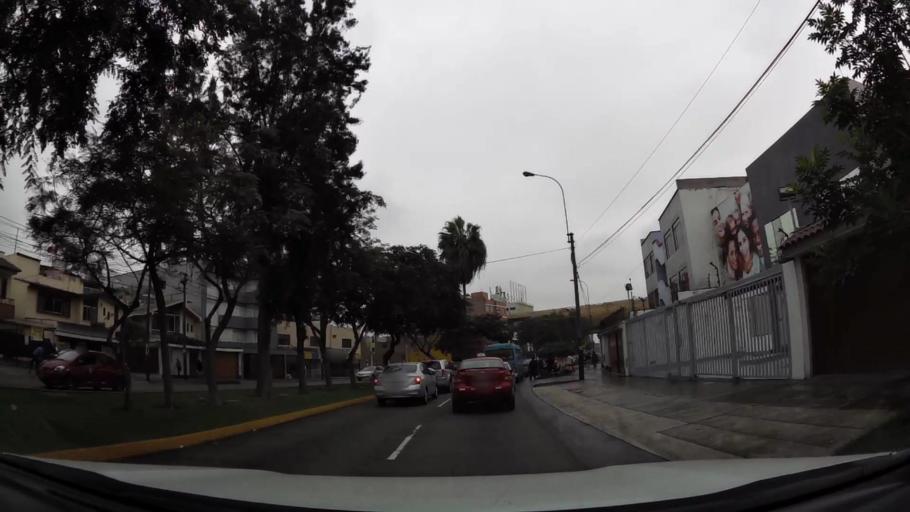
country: PE
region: Lima
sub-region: Lima
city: Surco
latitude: -12.1338
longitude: -76.9960
